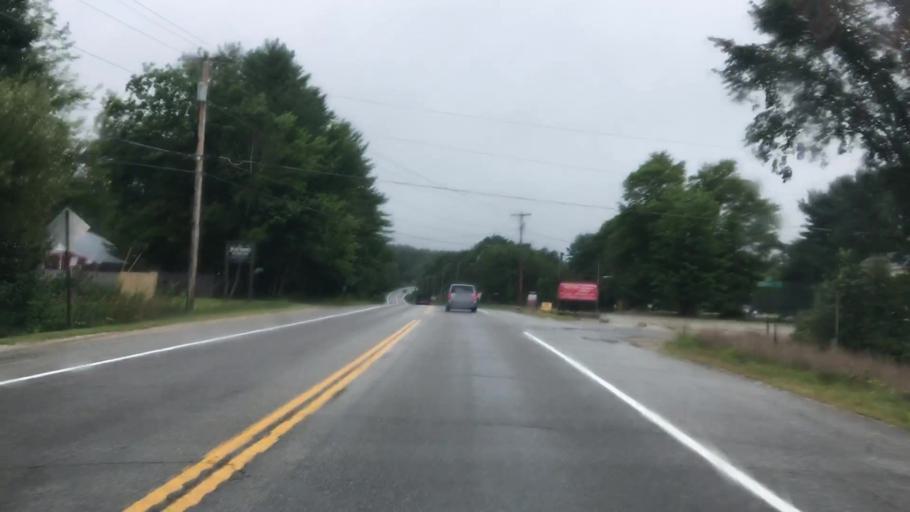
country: US
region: Maine
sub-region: Cumberland County
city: Raymond
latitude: 43.9572
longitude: -70.5616
